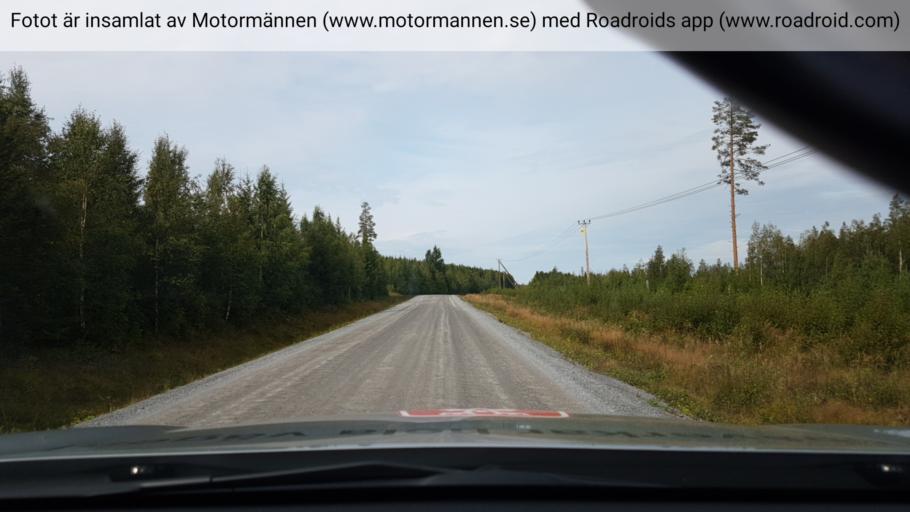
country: SE
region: Vaesterbotten
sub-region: Bjurholms Kommun
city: Bjurholm
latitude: 63.8891
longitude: 19.4228
